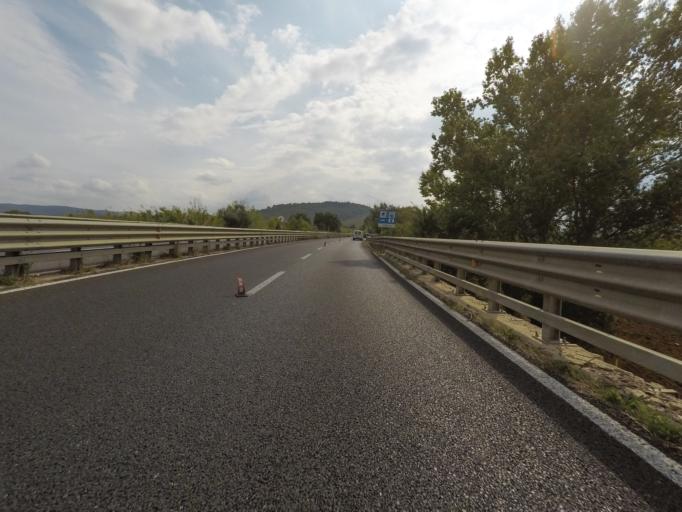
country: IT
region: Tuscany
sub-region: Provincia di Grosseto
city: Grosseto
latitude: 42.7151
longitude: 11.1437
